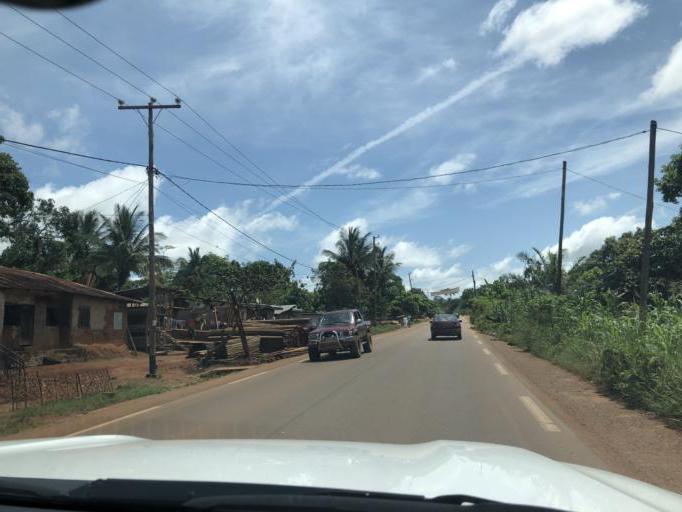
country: CM
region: Centre
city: Yaounde
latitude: 3.8623
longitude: 11.6194
